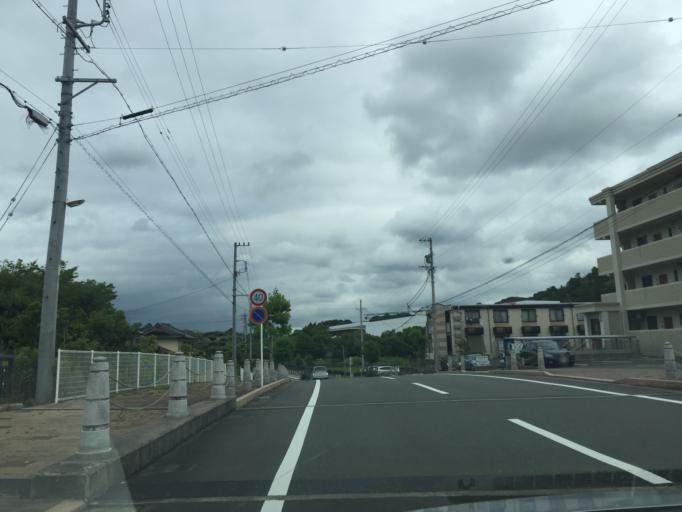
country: JP
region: Shizuoka
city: Fukuroi
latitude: 34.7507
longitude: 137.9657
